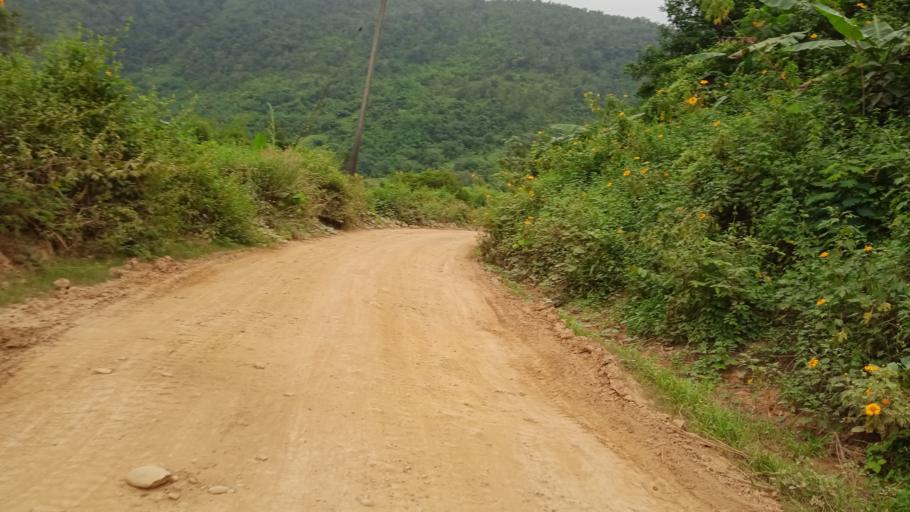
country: LA
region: Xiangkhoang
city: Phonsavan
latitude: 19.0941
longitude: 102.9880
